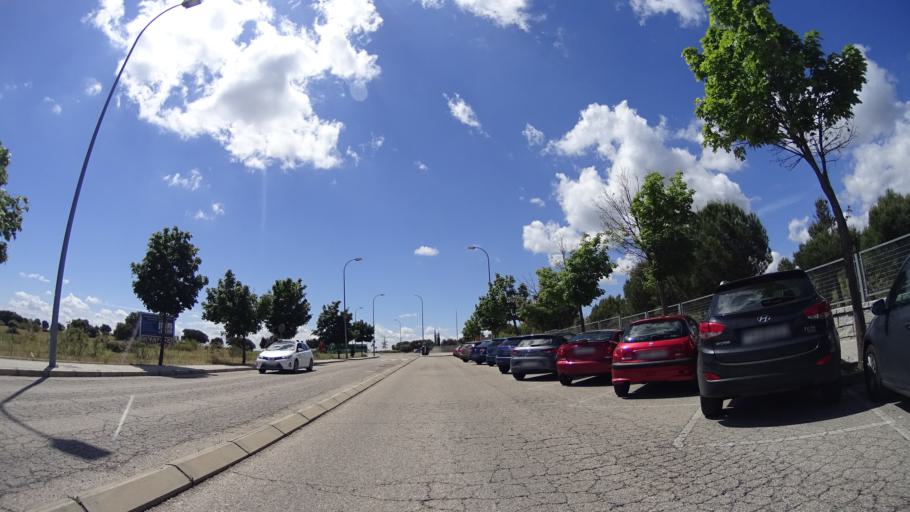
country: ES
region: Madrid
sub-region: Provincia de Madrid
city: Colmenarejo
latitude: 40.5436
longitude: -4.0112
